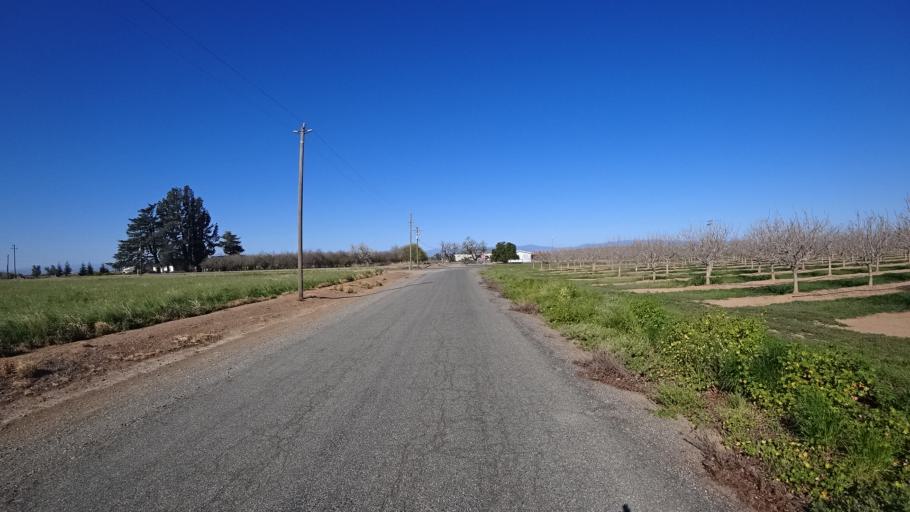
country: US
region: California
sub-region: Glenn County
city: Orland
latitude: 39.7442
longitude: -122.2471
